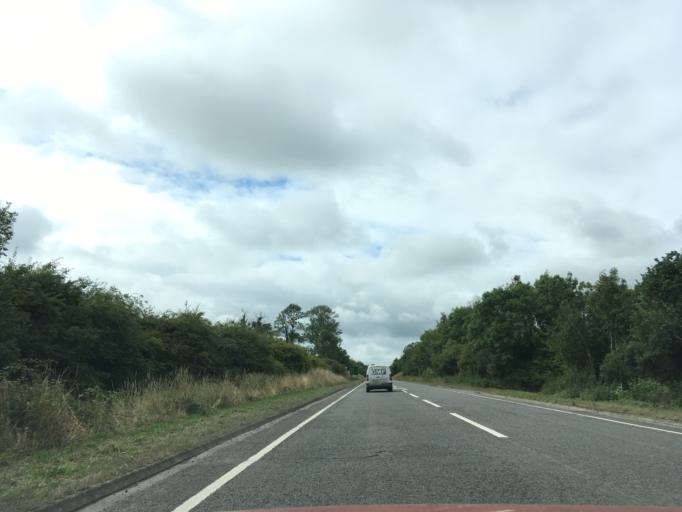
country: GB
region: Wales
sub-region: Carmarthenshire
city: Llandeilo
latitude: 51.8907
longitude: -4.0127
